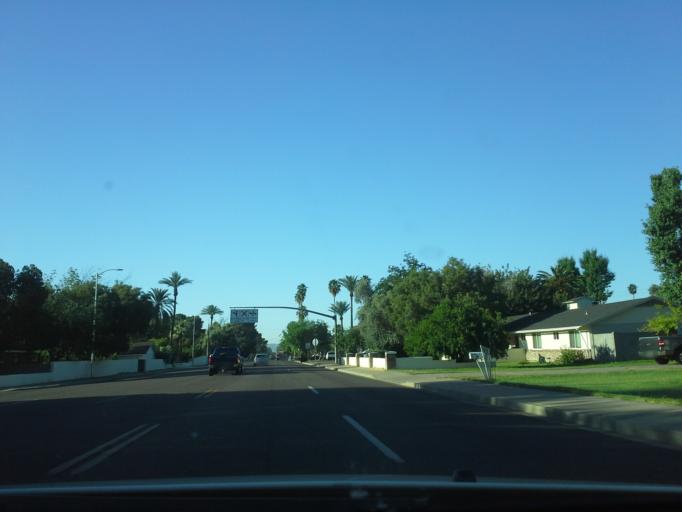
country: US
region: Arizona
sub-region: Maricopa County
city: Phoenix
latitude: 33.5484
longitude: -112.0826
